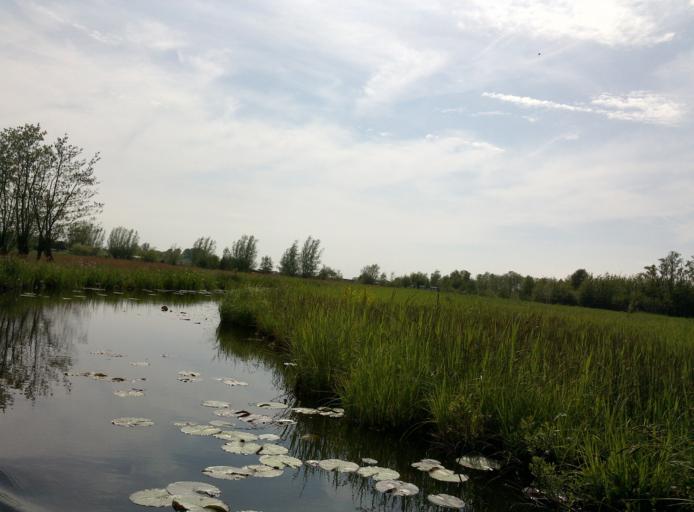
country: NL
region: South Holland
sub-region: Gemeente Nieuwkoop
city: Nieuwkoop
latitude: 52.1455
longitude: 4.8201
